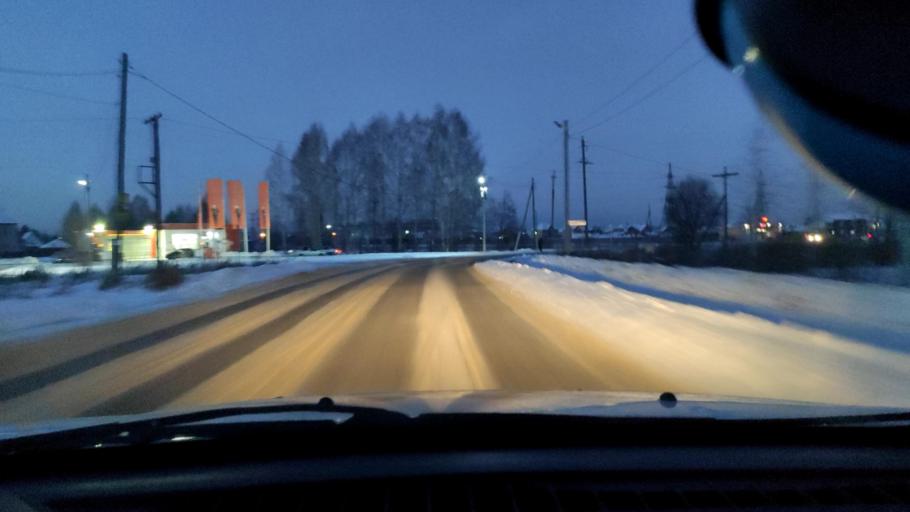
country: RU
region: Perm
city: Kultayevo
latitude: 57.8870
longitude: 55.9234
